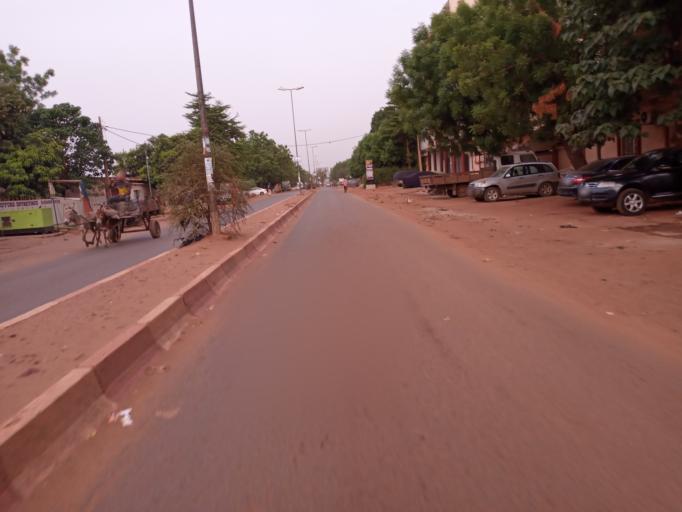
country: ML
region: Bamako
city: Bamako
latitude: 12.6629
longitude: -7.9737
